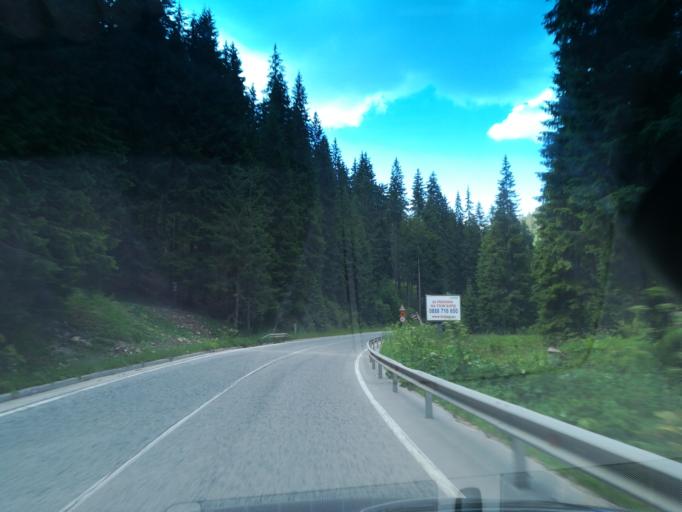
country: BG
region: Smolyan
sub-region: Obshtina Chepelare
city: Chepelare
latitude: 41.6663
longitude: 24.7143
